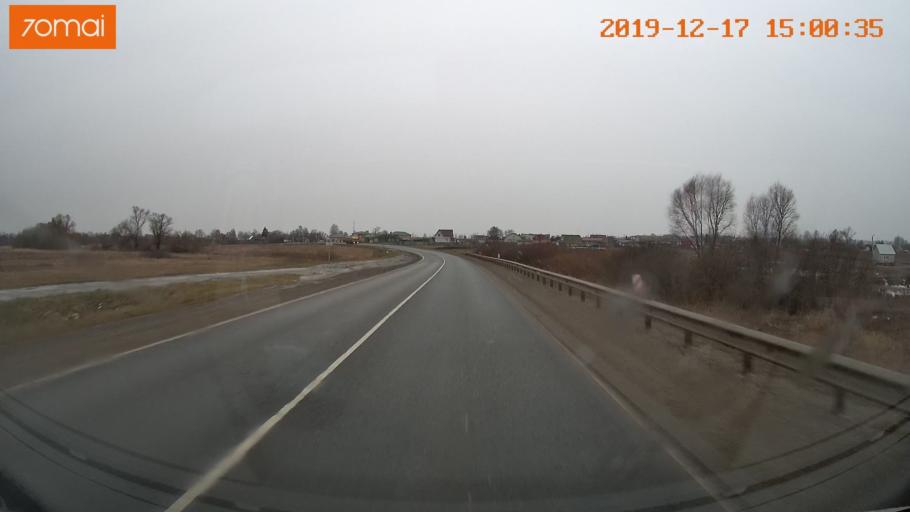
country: RU
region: Rjazan
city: Zakharovo
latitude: 54.2915
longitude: 39.1858
